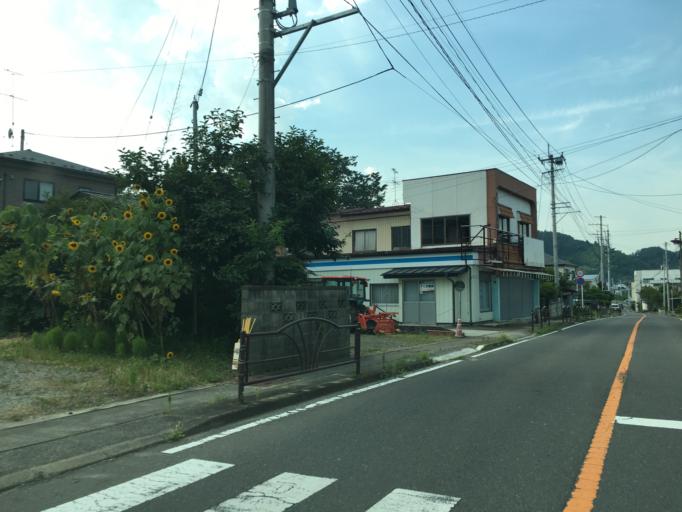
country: JP
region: Fukushima
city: Nihommatsu
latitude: 37.5588
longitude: 140.4130
